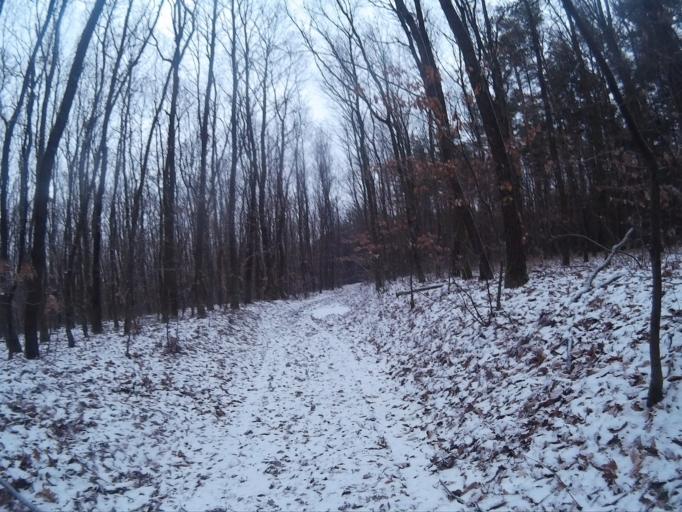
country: HU
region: Borsod-Abauj-Zemplen
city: Szendro
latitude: 48.3885
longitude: 20.8991
